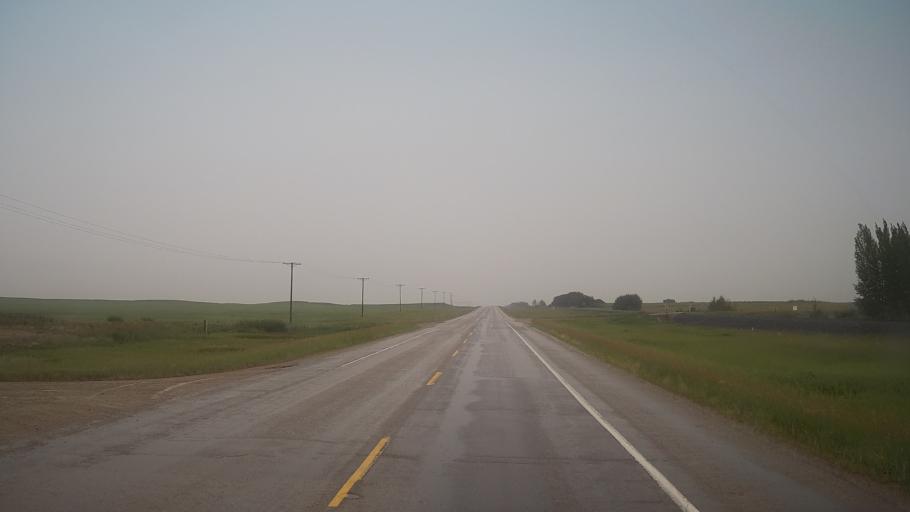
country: CA
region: Saskatchewan
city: Biggar
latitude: 52.0894
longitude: -108.0489
